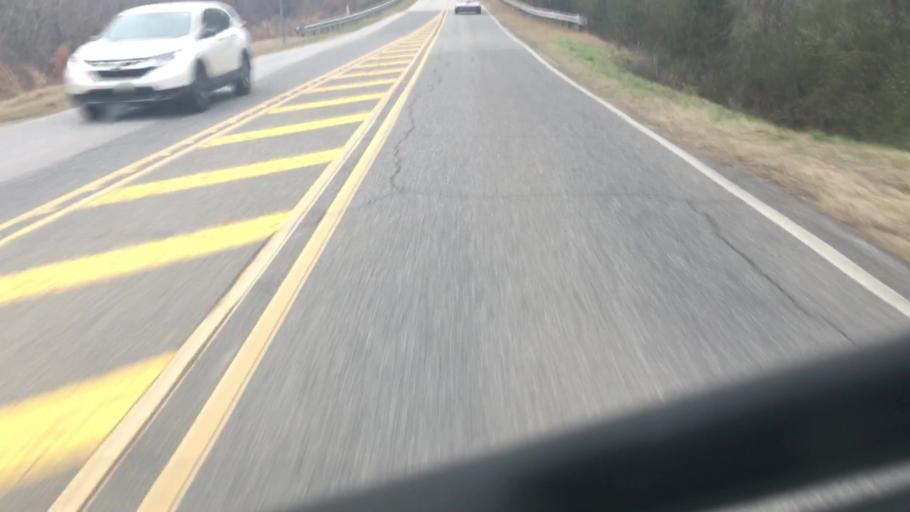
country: US
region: Alabama
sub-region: Jefferson County
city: Hoover
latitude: 33.3610
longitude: -86.8118
